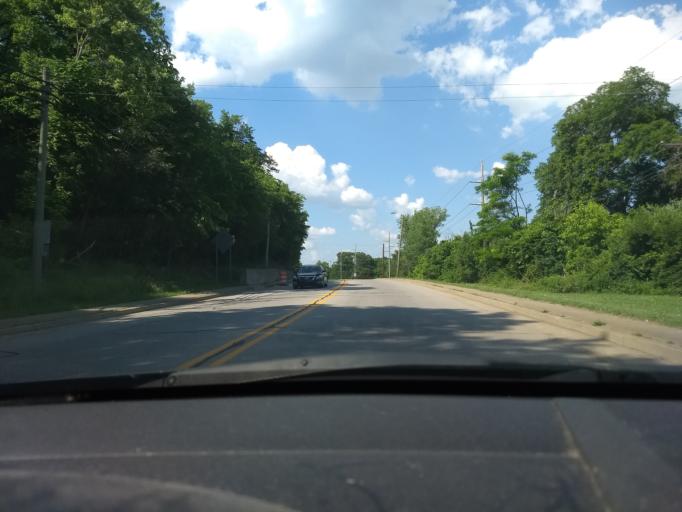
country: US
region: Indiana
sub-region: Floyd County
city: New Albany
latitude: 38.2759
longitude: -85.8357
